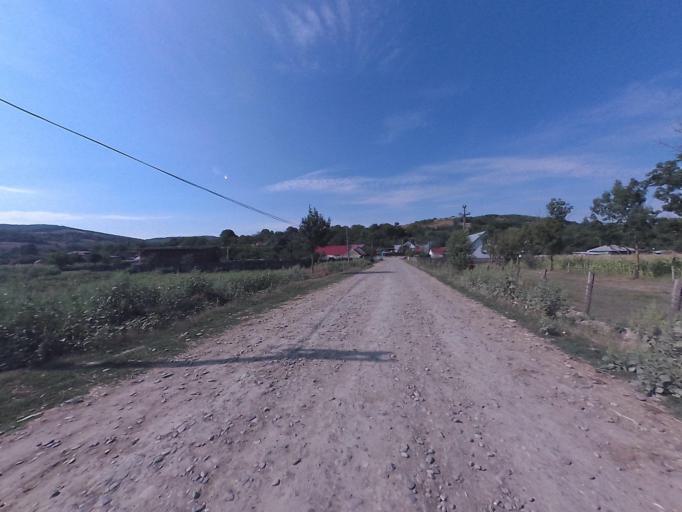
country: RO
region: Vaslui
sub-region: Comuna Osesti
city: Buda
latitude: 46.7607
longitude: 27.4266
